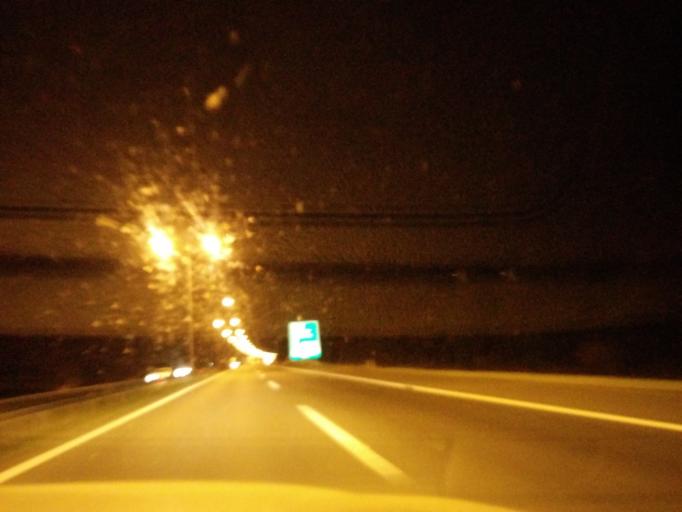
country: RS
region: Central Serbia
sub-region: Belgrade
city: Surcin
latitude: 44.8337
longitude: 20.2970
